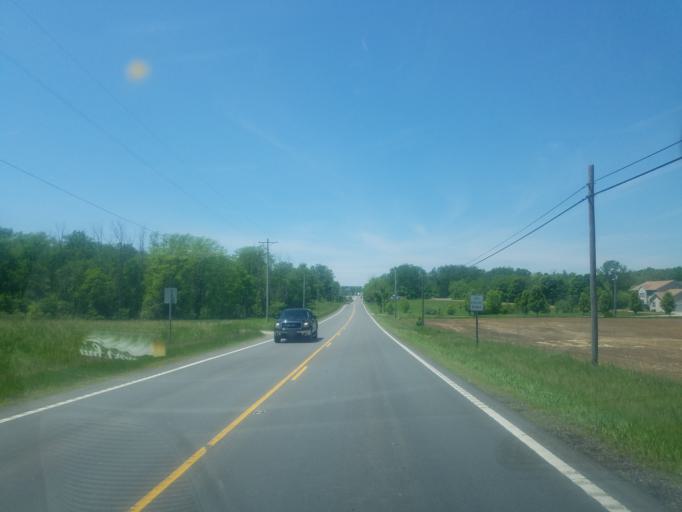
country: US
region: Ohio
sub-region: Huron County
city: New London
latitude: 41.0293
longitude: -82.4093
